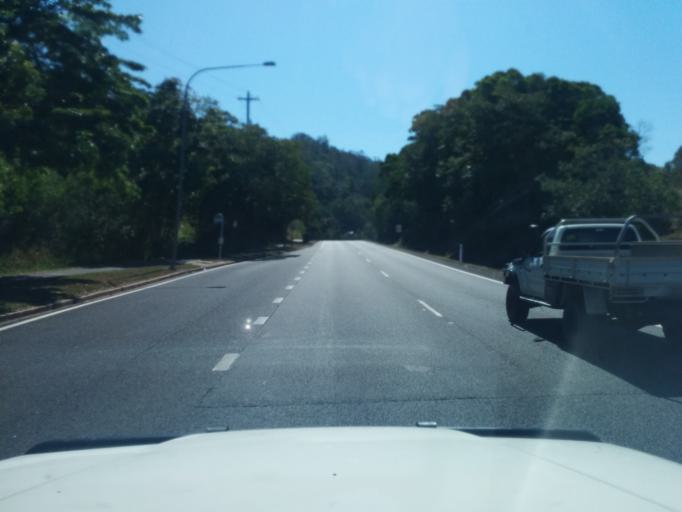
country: AU
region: Queensland
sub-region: Cairns
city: Redlynch
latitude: -16.9136
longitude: 145.7209
